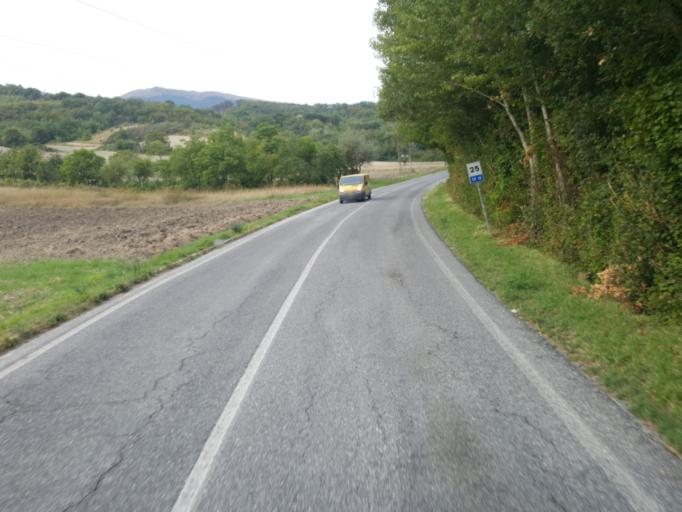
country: IT
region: Umbria
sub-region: Provincia di Perugia
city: Fossato di Vico
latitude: 43.3135
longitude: 12.8351
